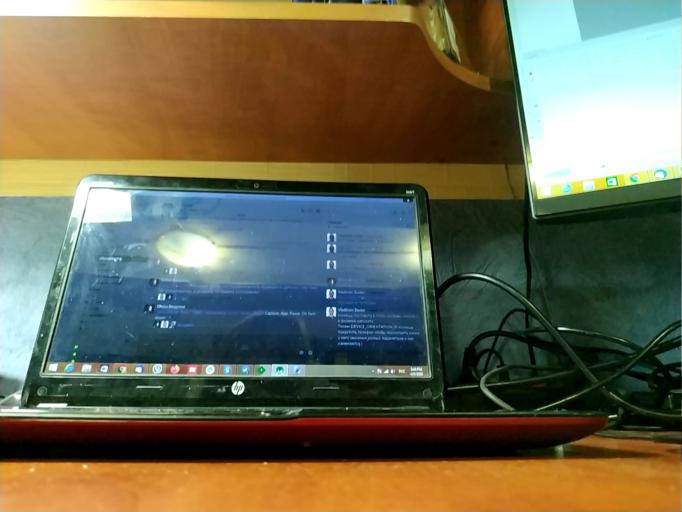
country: RU
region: Tverskaya
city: Sandovo
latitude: 58.5974
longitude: 36.4174
